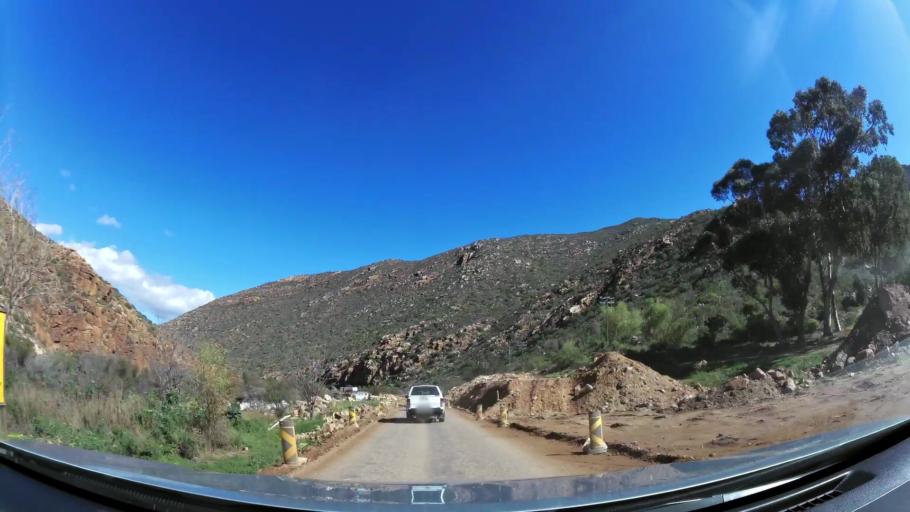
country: ZA
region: Western Cape
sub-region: Cape Winelands District Municipality
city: Ashton
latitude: -33.8121
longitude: 20.0922
